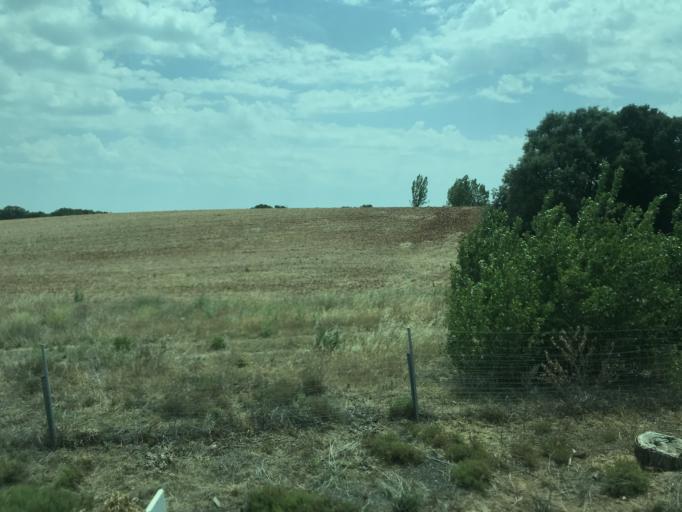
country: ES
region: Castille and Leon
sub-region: Provincia de Burgos
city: Villalmanzo
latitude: 42.0807
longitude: -3.7315
